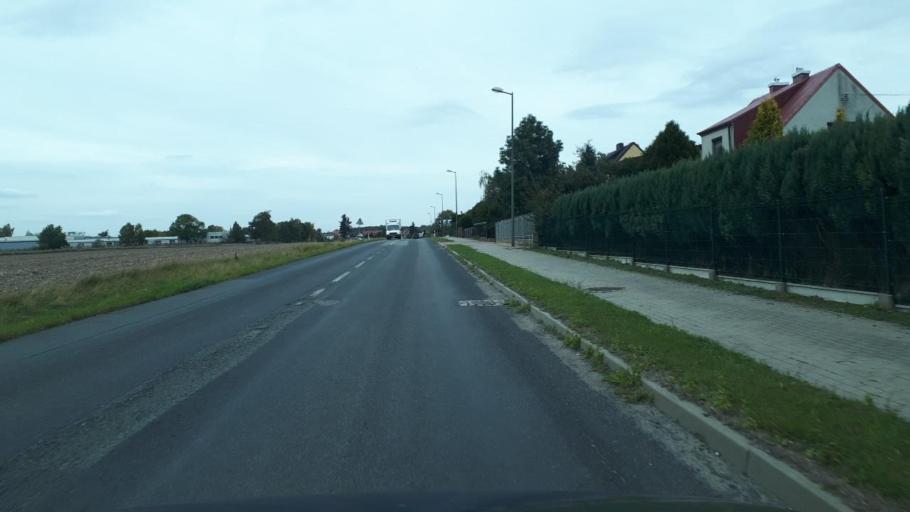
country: PL
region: Opole Voivodeship
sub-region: Powiat oleski
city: Dobrodzien
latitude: 50.7131
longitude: 18.4465
